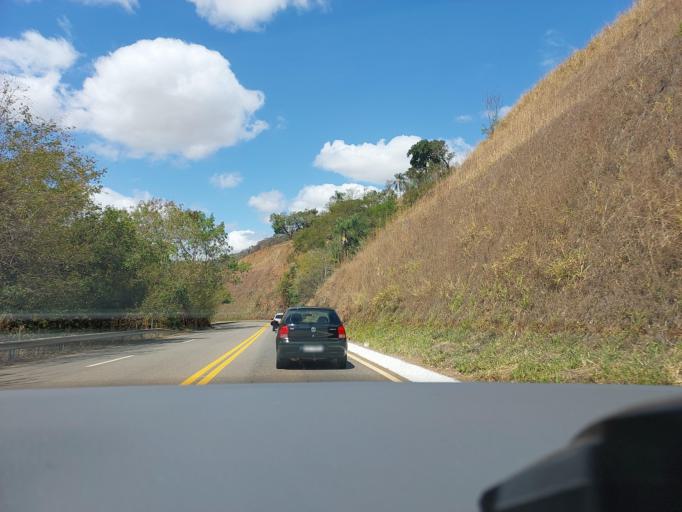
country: BR
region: Minas Gerais
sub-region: Muriae
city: Muriae
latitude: -21.0940
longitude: -42.4727
